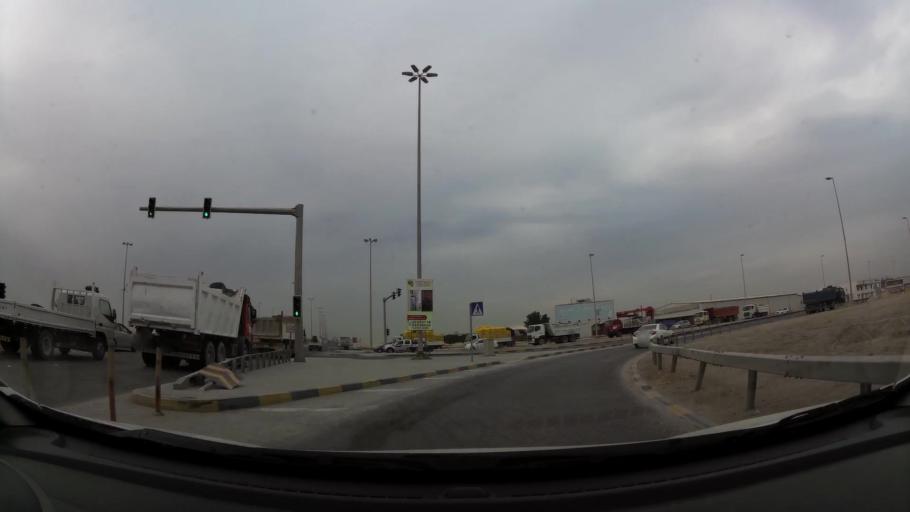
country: BH
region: Northern
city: Sitrah
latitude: 26.1720
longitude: 50.6011
